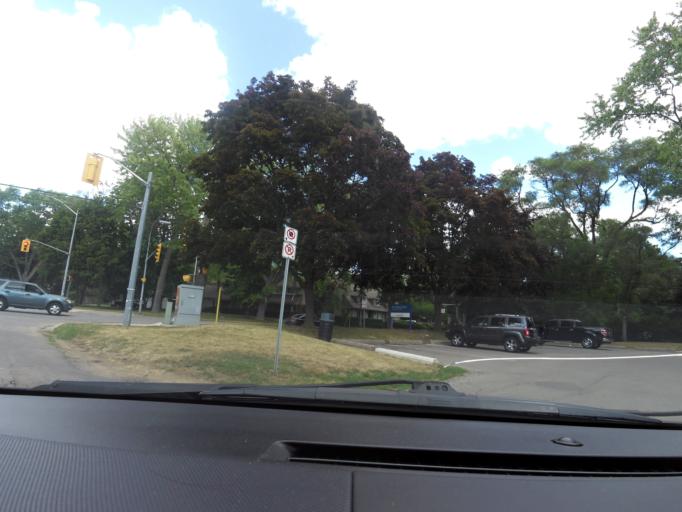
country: CA
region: Ontario
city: Burlington
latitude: 43.3330
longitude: -79.7780
